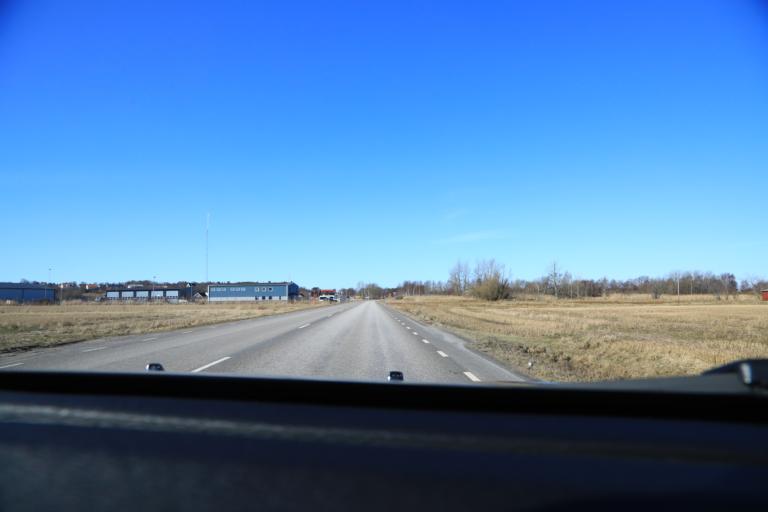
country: SE
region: Halland
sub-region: Kungsbacka Kommun
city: Frillesas
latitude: 57.2352
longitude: 12.1382
